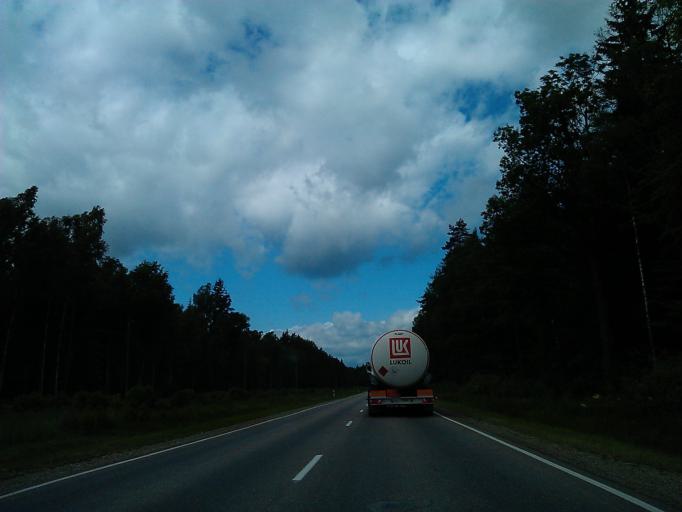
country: LV
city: Tireli
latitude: 56.9317
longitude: 23.4990
